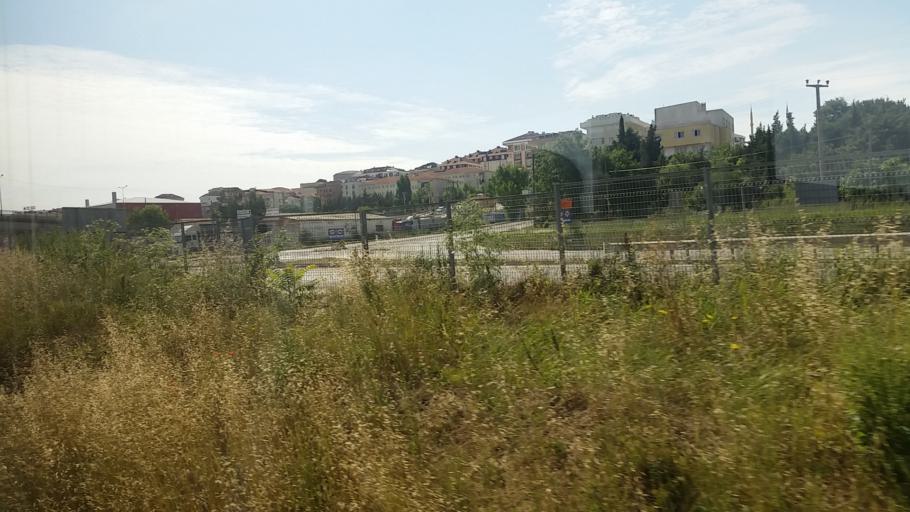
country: TR
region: Tekirdag
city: Cerkezkoey
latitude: 41.2793
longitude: 27.9997
